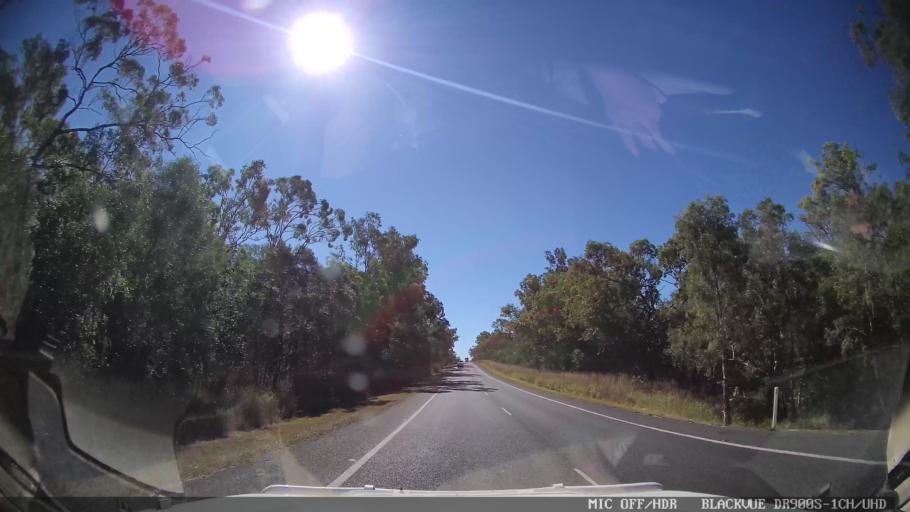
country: AU
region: Queensland
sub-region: Gladstone
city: Toolooa
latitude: -23.9691
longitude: 151.2174
